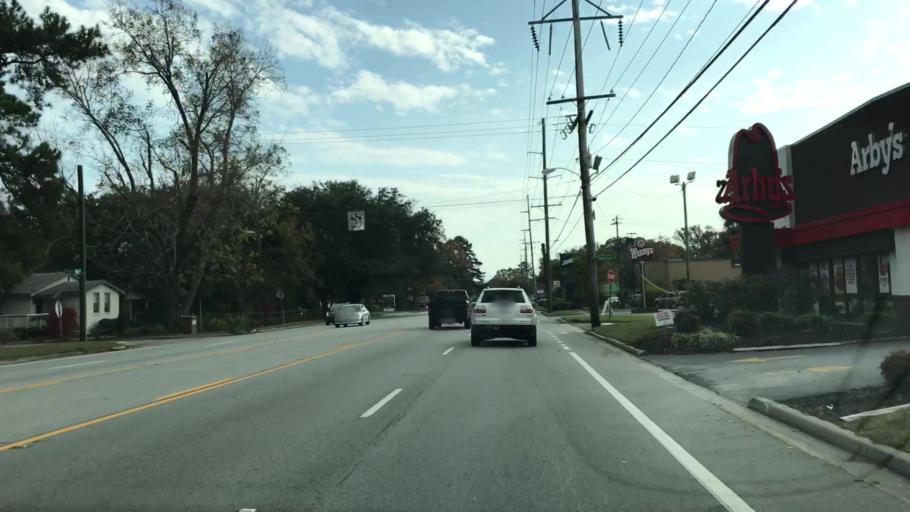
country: US
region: South Carolina
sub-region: Charleston County
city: Charleston
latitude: 32.7586
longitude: -79.9740
